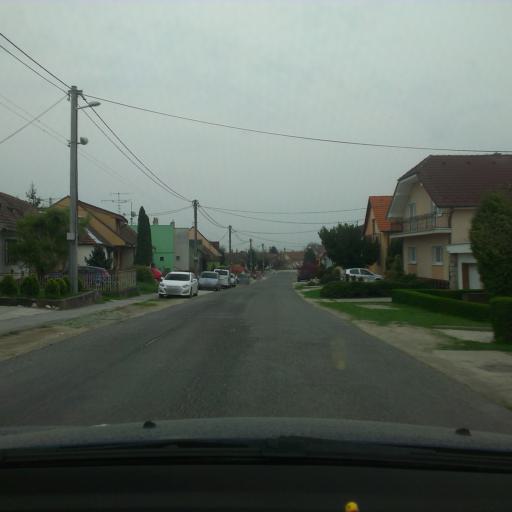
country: SK
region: Trnavsky
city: Vrbove
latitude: 48.5935
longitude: 17.7537
